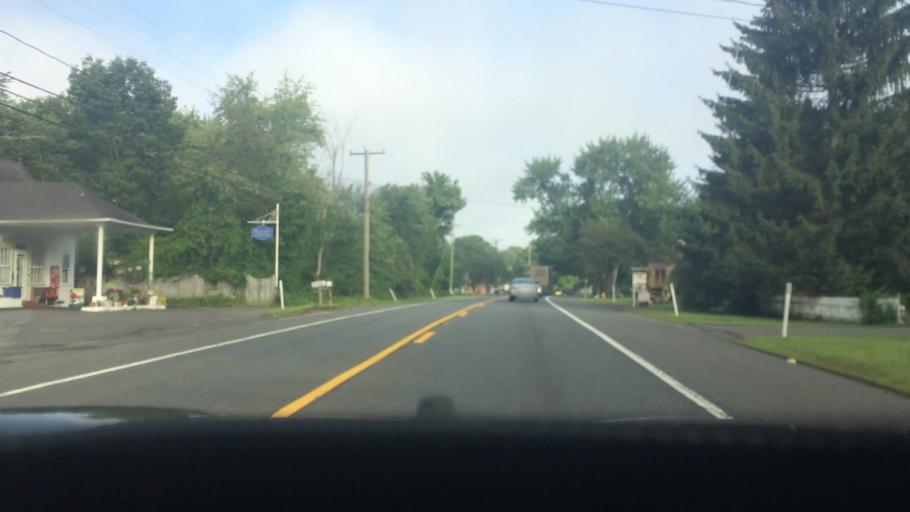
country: US
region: Massachusetts
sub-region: Franklin County
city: Turners Falls
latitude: 42.6097
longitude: -72.5414
